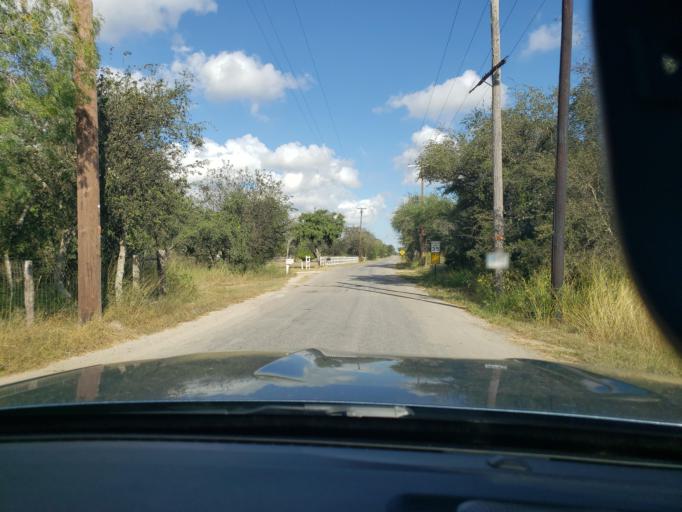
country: US
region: Texas
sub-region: Bee County
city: Beeville
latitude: 28.4398
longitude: -97.7124
